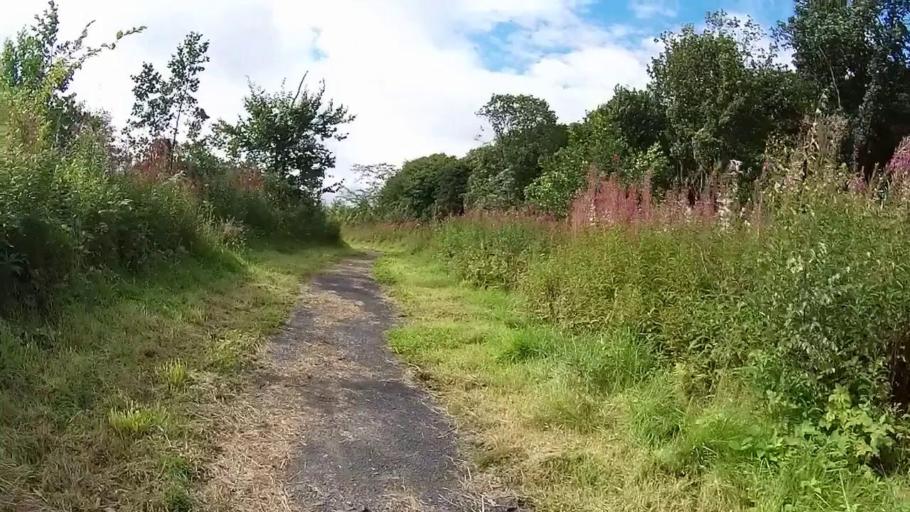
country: GB
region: Scotland
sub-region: Fife
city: Glenrothes
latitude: 56.2187
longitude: -3.1677
